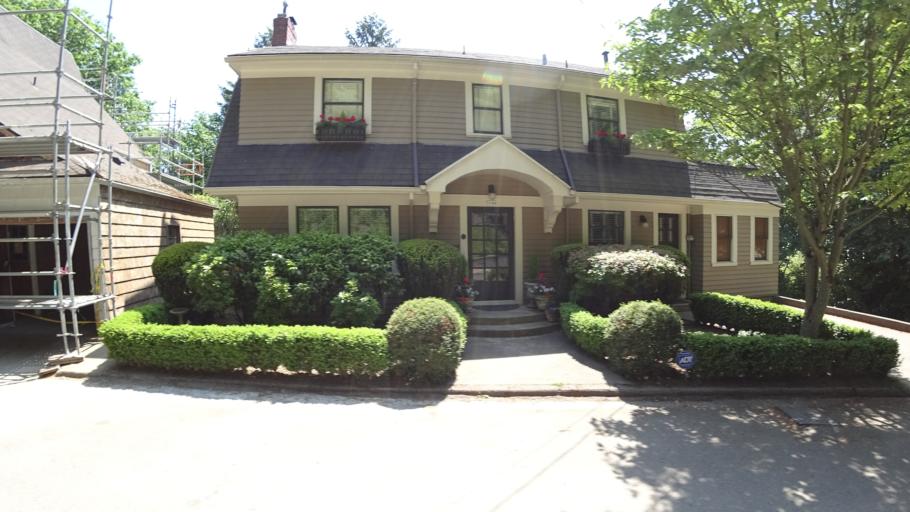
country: US
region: Oregon
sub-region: Multnomah County
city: Portland
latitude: 45.5193
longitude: -122.7132
